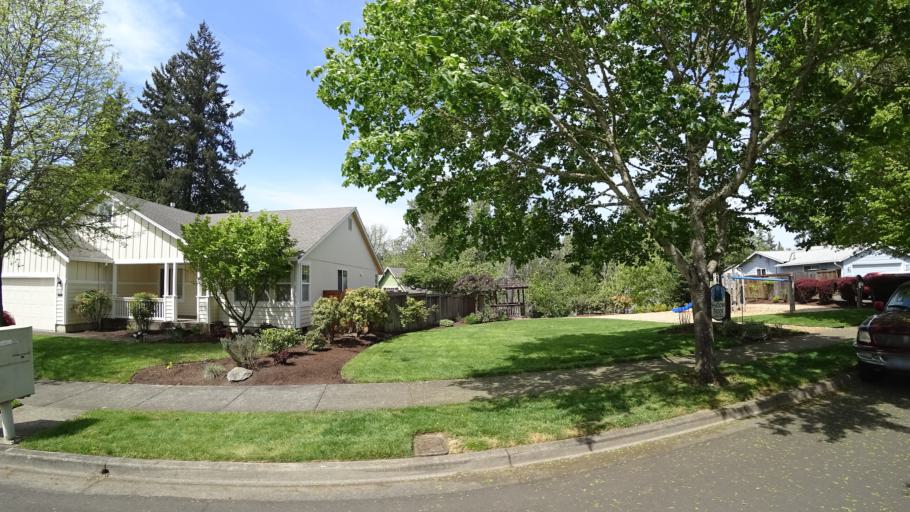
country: US
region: Oregon
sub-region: Washington County
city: Rockcreek
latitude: 45.5154
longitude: -122.9249
